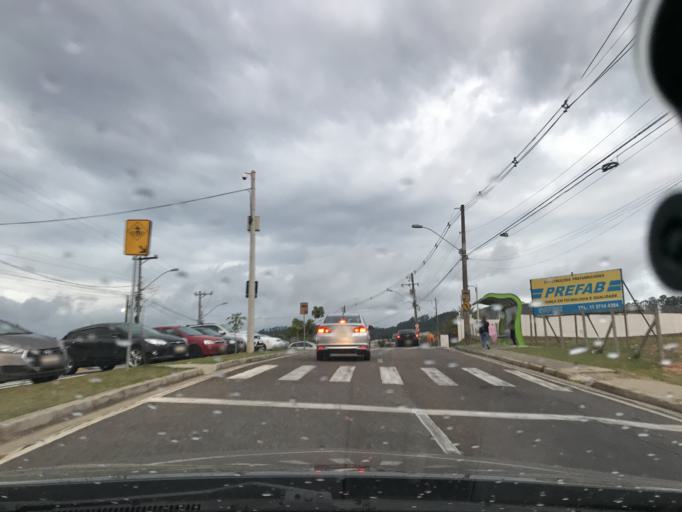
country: BR
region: Sao Paulo
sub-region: Carapicuiba
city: Carapicuiba
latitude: -23.4911
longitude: -46.8301
